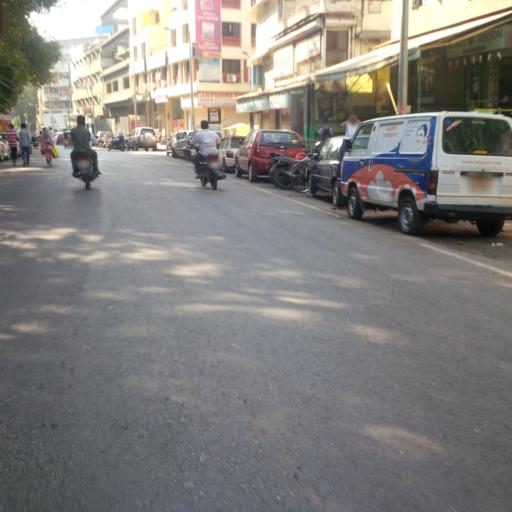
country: IN
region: Maharashtra
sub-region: Pune Division
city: Pune
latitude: 18.5139
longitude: 73.8468
